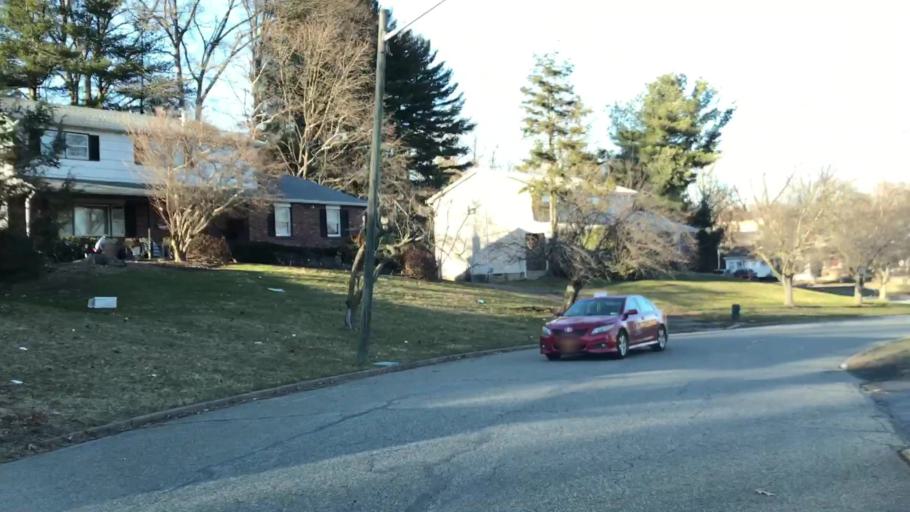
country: US
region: New York
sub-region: Rockland County
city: Hillcrest
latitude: 41.1343
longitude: -74.0404
